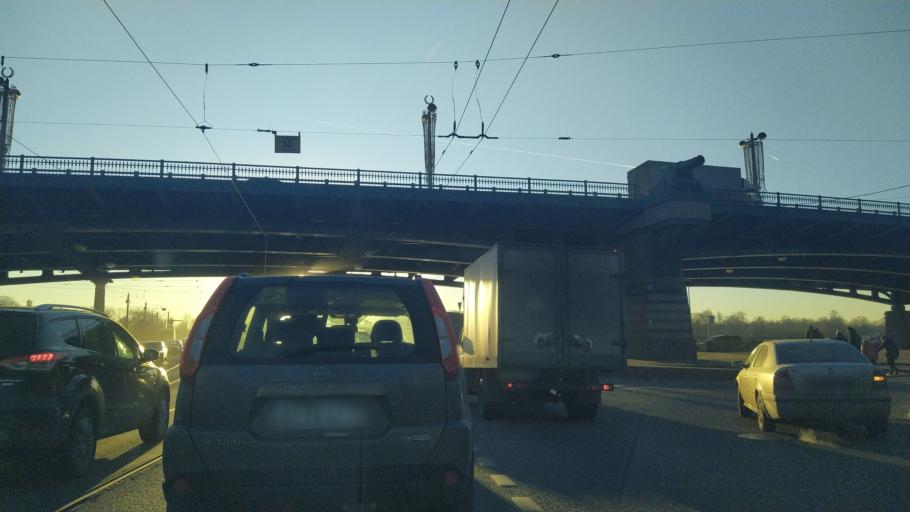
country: RU
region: Leningrad
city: Chernaya Rechka
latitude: 59.9842
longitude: 30.3008
